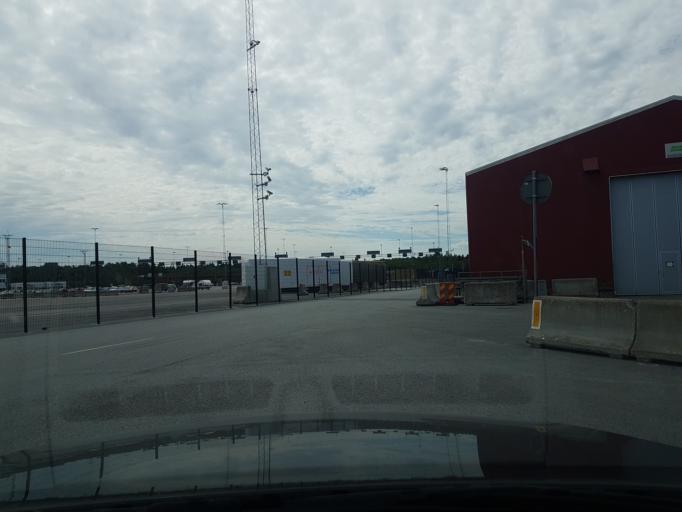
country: SE
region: Stockholm
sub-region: Norrtalje Kommun
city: Bjorko
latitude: 59.7240
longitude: 19.0650
